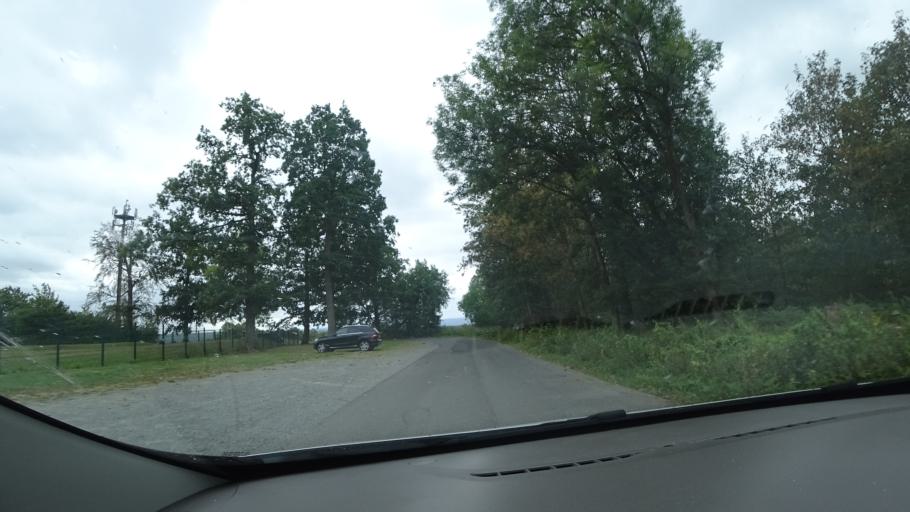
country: DE
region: Rheinland-Pfalz
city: Hohr-Grenzhausen
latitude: 50.4481
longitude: 7.6635
